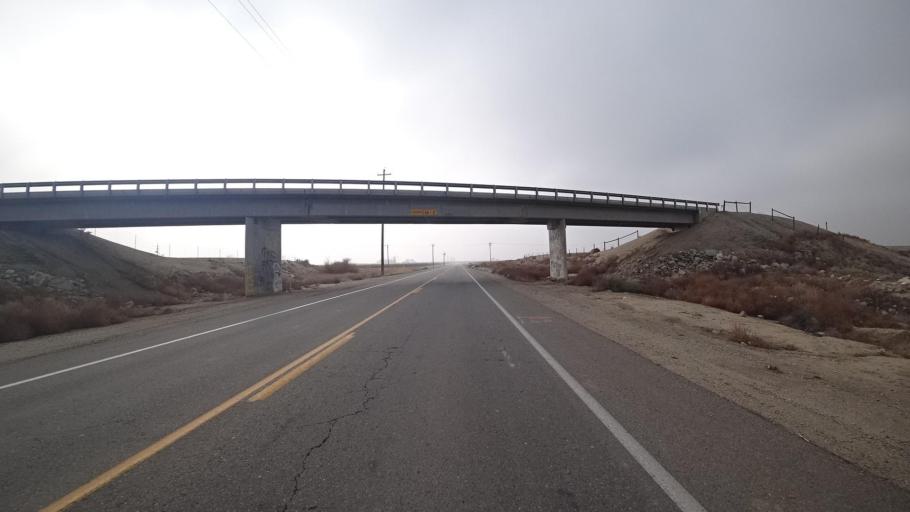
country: US
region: California
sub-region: Kern County
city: Pine Mountain Club
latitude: 35.0676
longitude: -119.1327
